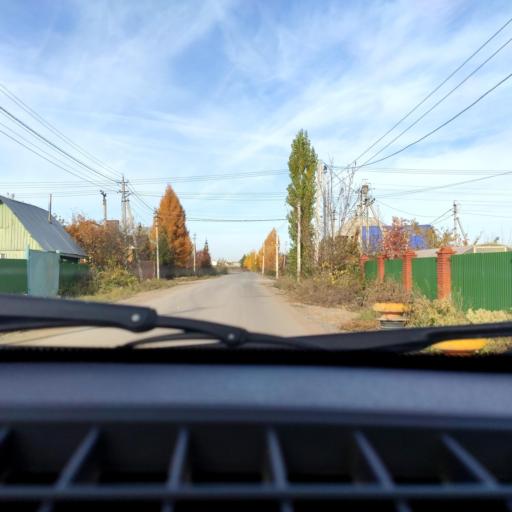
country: RU
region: Bashkortostan
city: Ufa
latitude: 54.6427
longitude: 55.9231
